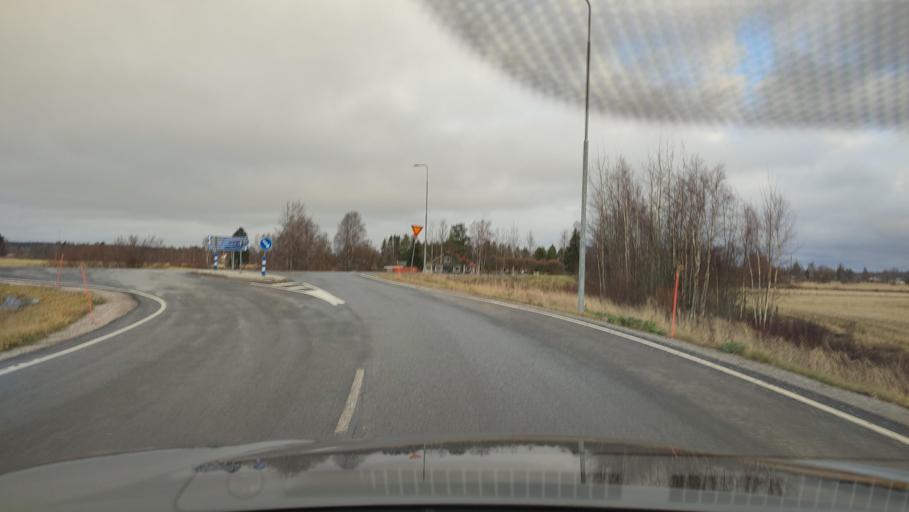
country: FI
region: Southern Ostrobothnia
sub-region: Suupohja
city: Kauhajoki
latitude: 62.3495
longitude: 22.0495
